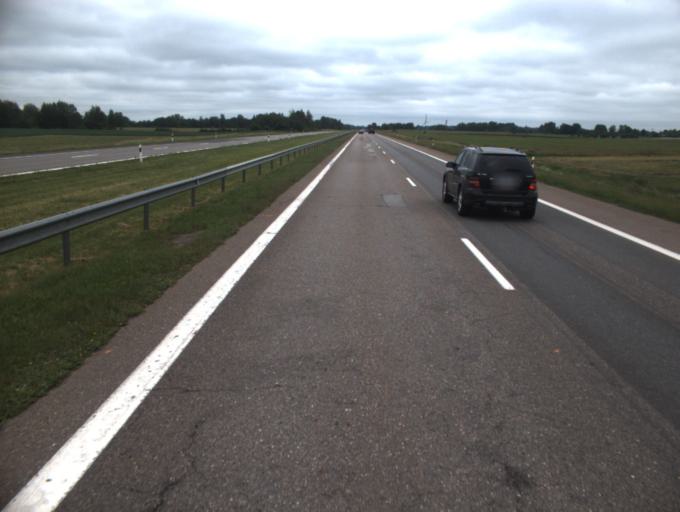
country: LT
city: Skaudvile
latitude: 55.4278
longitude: 22.7563
